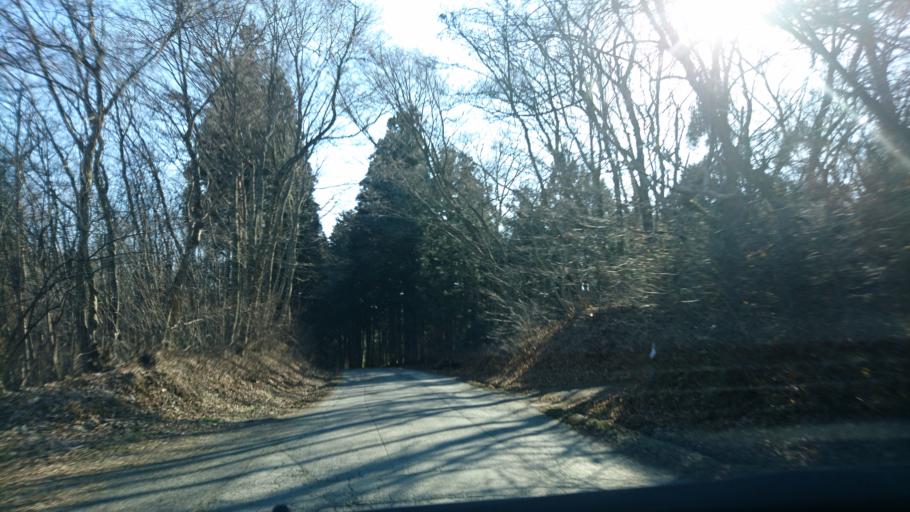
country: JP
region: Iwate
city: Ichinoseki
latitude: 38.8098
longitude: 141.2664
